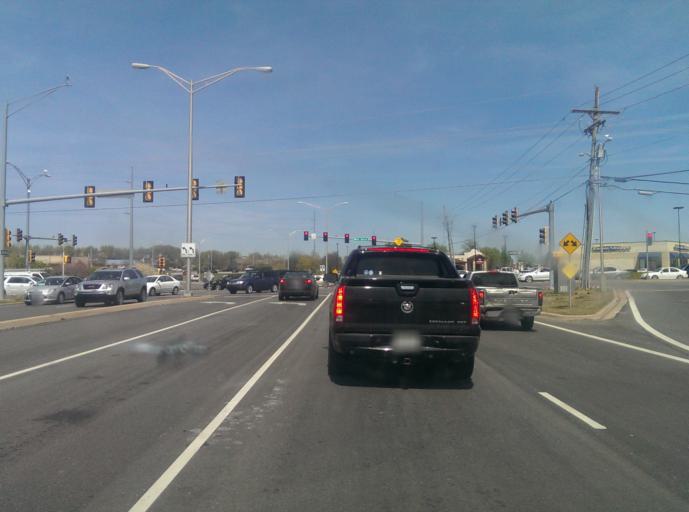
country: US
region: Kansas
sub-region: Johnson County
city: Overland Park
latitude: 38.9124
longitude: -94.6677
